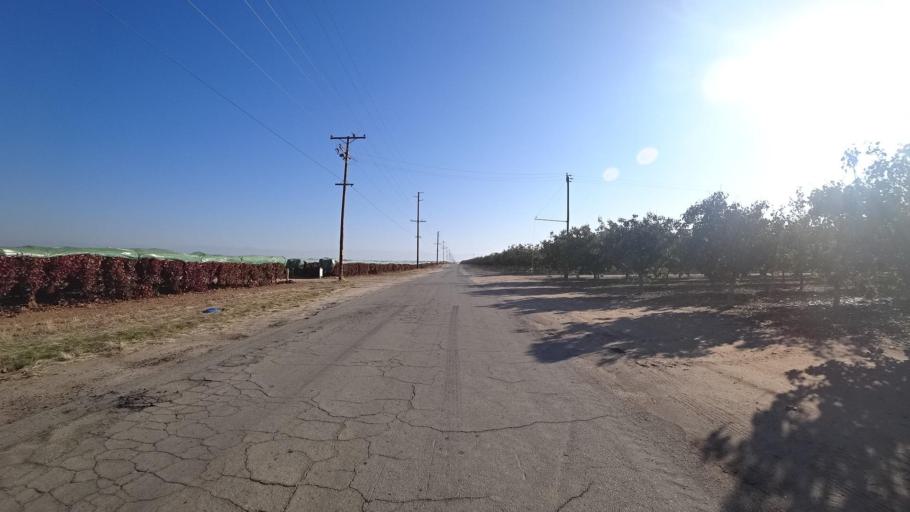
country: US
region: California
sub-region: Tulare County
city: Richgrove
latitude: 35.7326
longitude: -119.1211
